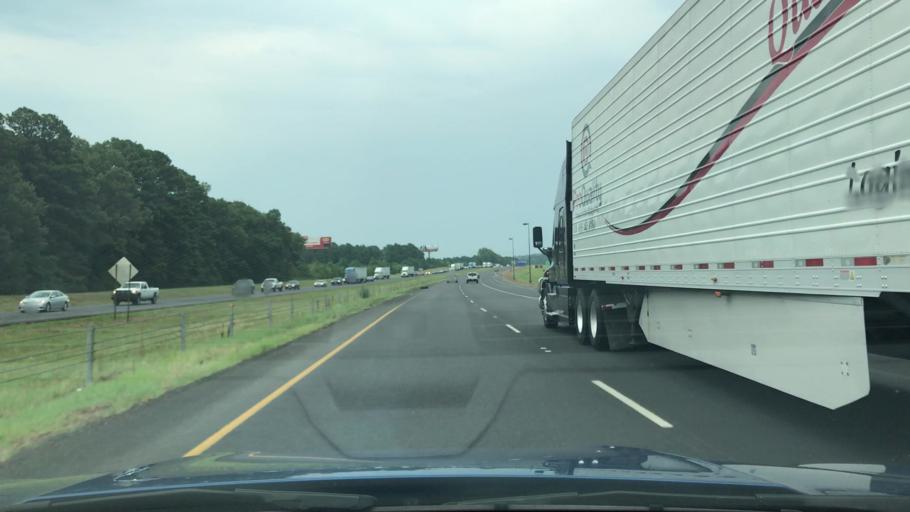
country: US
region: Louisiana
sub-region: Caddo Parish
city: Greenwood
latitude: 32.4513
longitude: -93.9975
